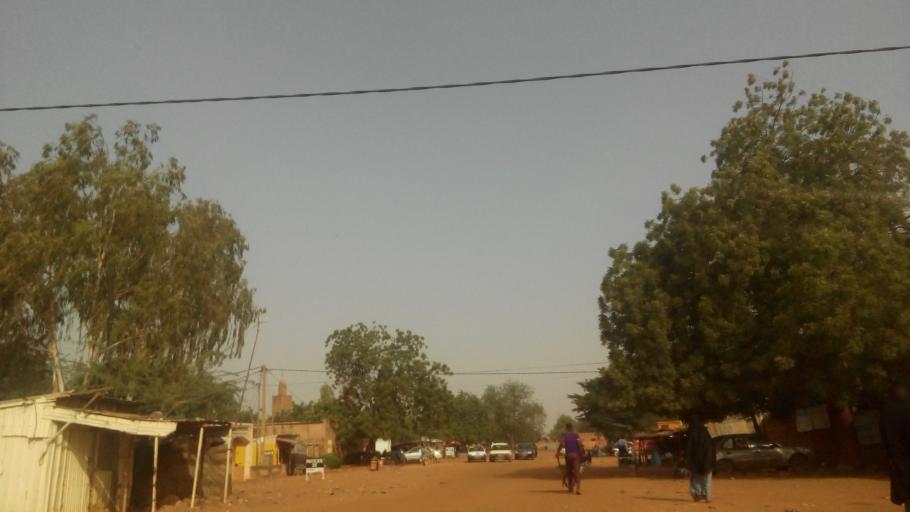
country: NE
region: Niamey
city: Niamey
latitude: 13.5290
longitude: 2.0875
